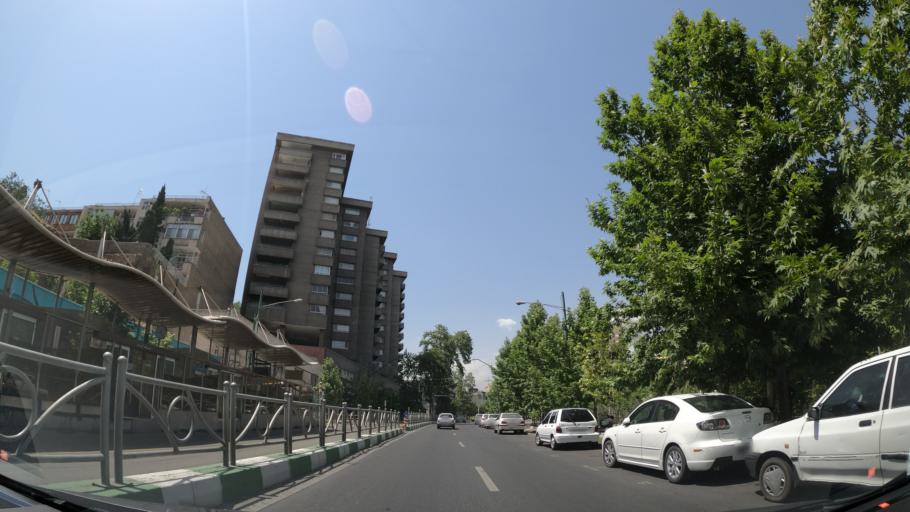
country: IR
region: Tehran
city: Tehran
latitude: 35.7367
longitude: 51.4093
